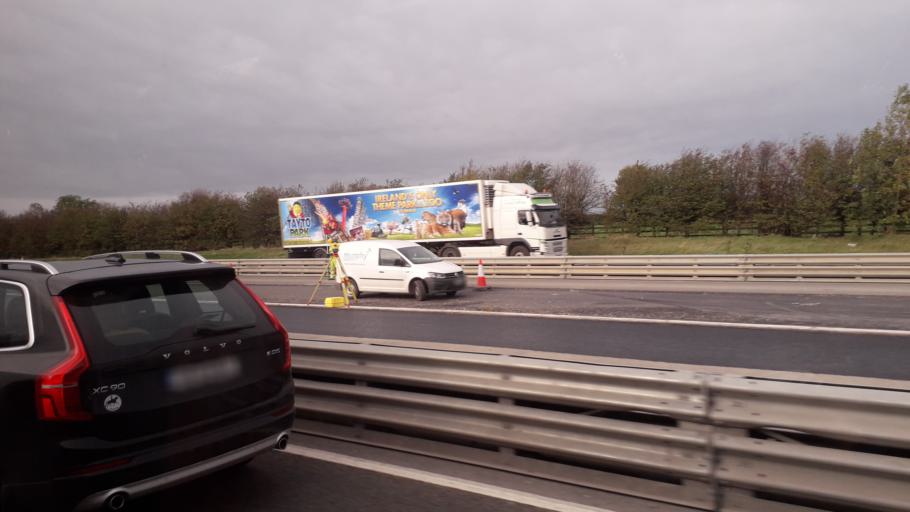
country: IE
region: Leinster
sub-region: Kildare
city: Naas
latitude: 53.2305
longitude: -6.6908
